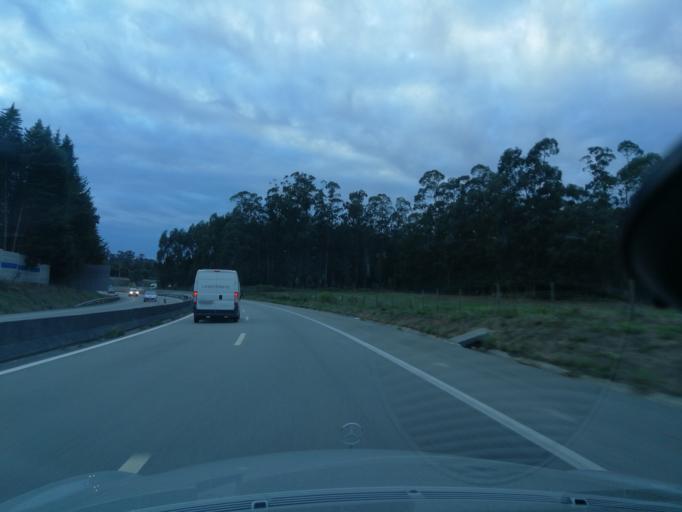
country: PT
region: Aveiro
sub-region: Albergaria-A-Velha
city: Albergaria-a-Velha
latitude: 40.6889
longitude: -8.5165
